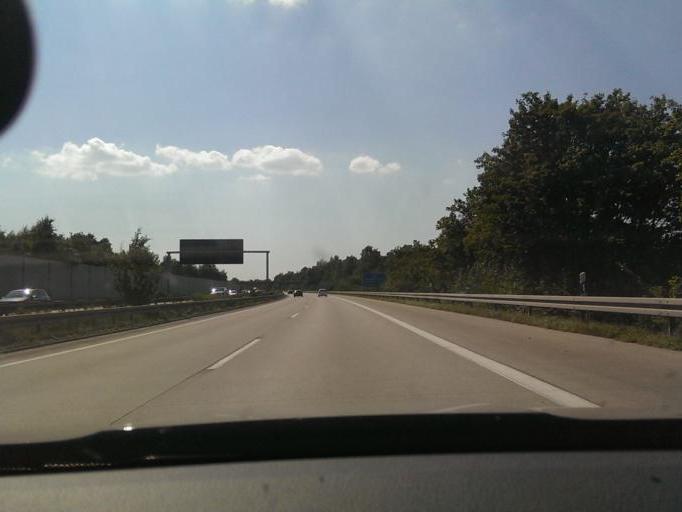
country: DE
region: Lower Saxony
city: Langenhagen
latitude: 52.4862
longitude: 9.7237
